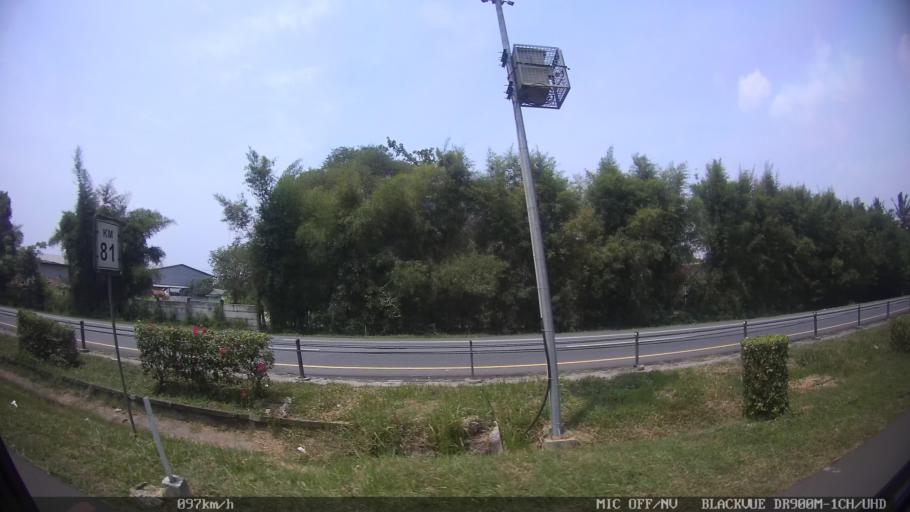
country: ID
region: Banten
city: Serang
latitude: -6.0652
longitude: 106.1253
